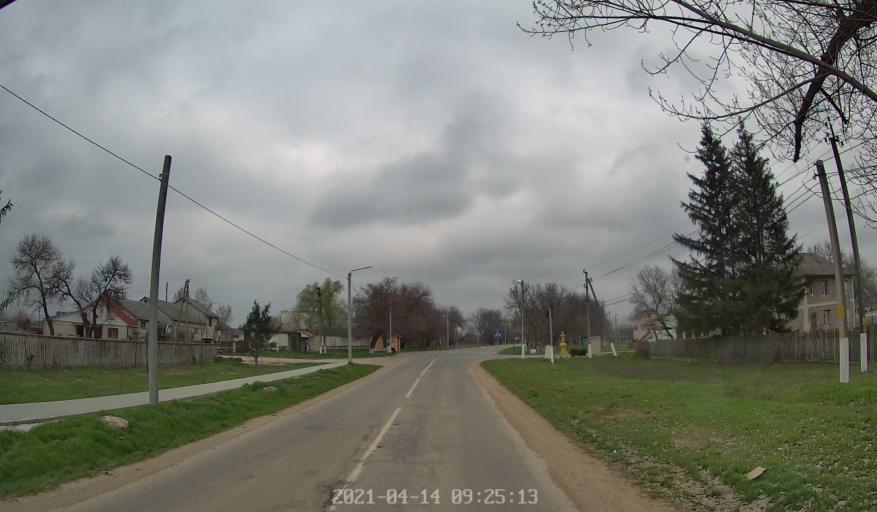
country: MD
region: Chisinau
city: Vadul lui Voda
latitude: 47.1141
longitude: 29.1113
